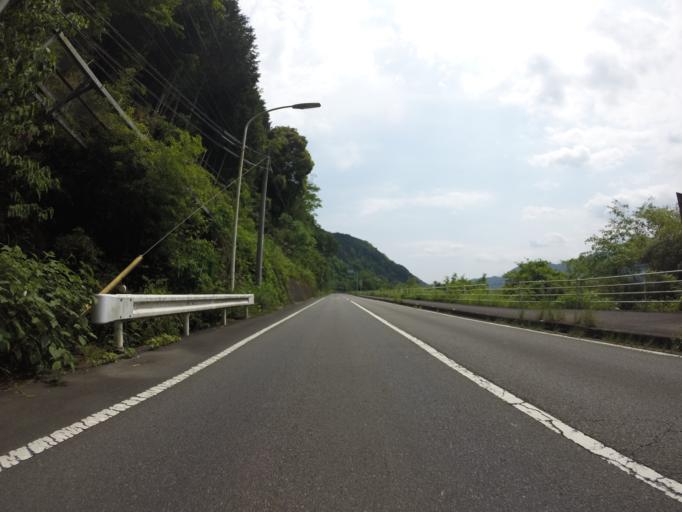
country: JP
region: Shizuoka
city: Shizuoka-shi
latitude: 35.0853
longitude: 138.3761
